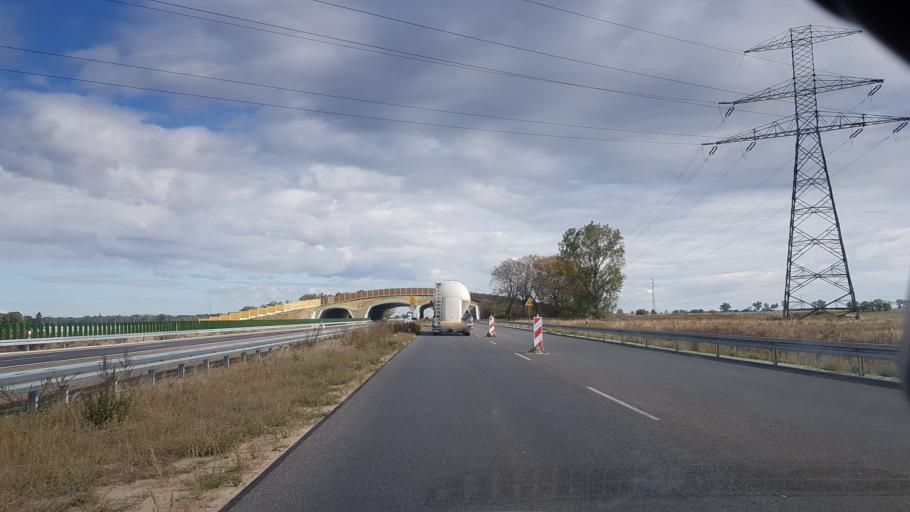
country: PL
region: Greater Poland Voivodeship
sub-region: Powiat poznanski
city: Steszew
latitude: 52.3149
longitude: 16.7088
